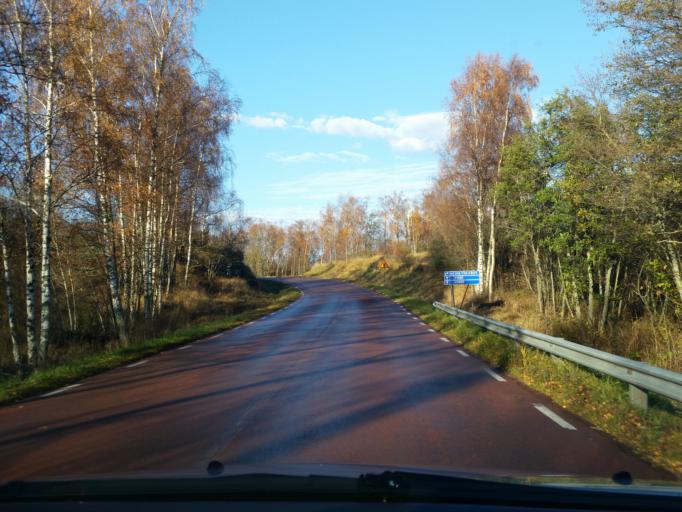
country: AX
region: Alands skaergard
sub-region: Braendoe
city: Braendoe
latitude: 60.4327
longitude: 21.0478
